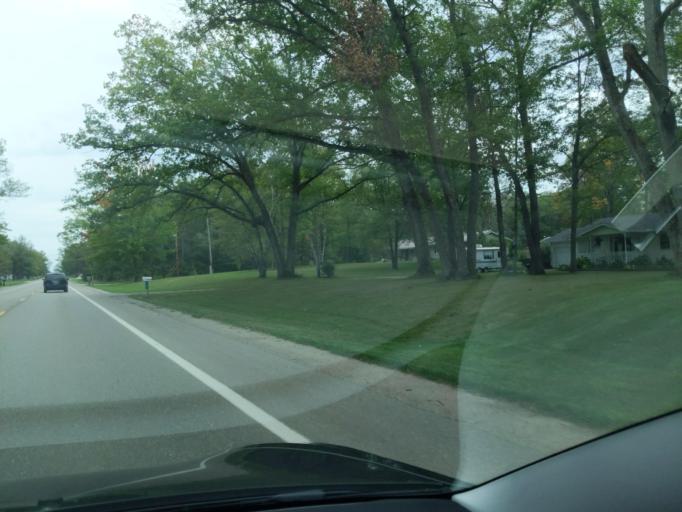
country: US
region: Michigan
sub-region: Clare County
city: Clare
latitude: 43.8520
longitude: -84.8944
